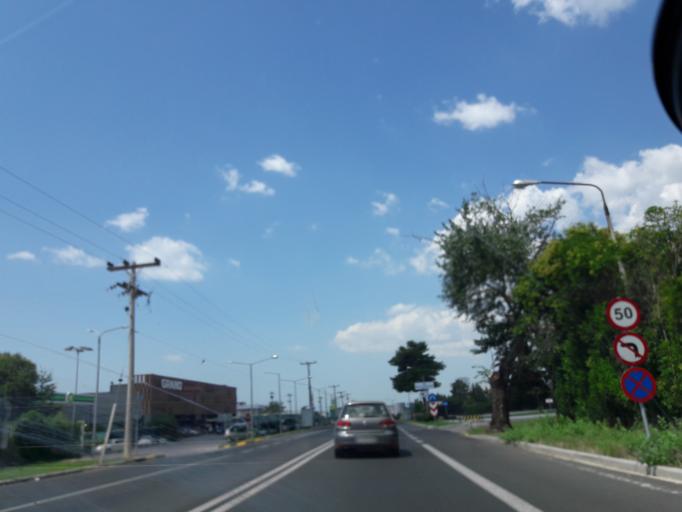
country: GR
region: Central Macedonia
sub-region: Nomos Thessalonikis
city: Thermi
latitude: 40.5394
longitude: 23.0321
